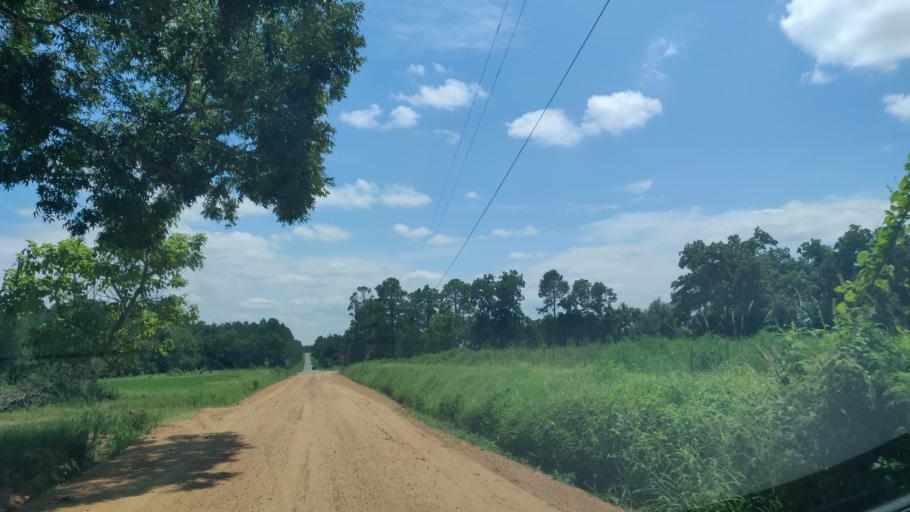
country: US
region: Georgia
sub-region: Tift County
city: Omega
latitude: 31.4616
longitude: -83.6374
